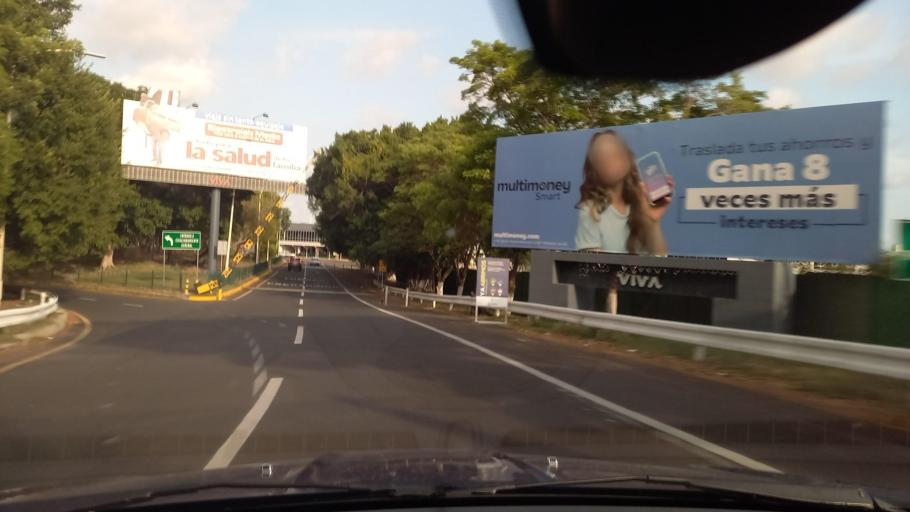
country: SV
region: La Paz
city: El Rosario
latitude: 13.4458
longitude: -89.0601
